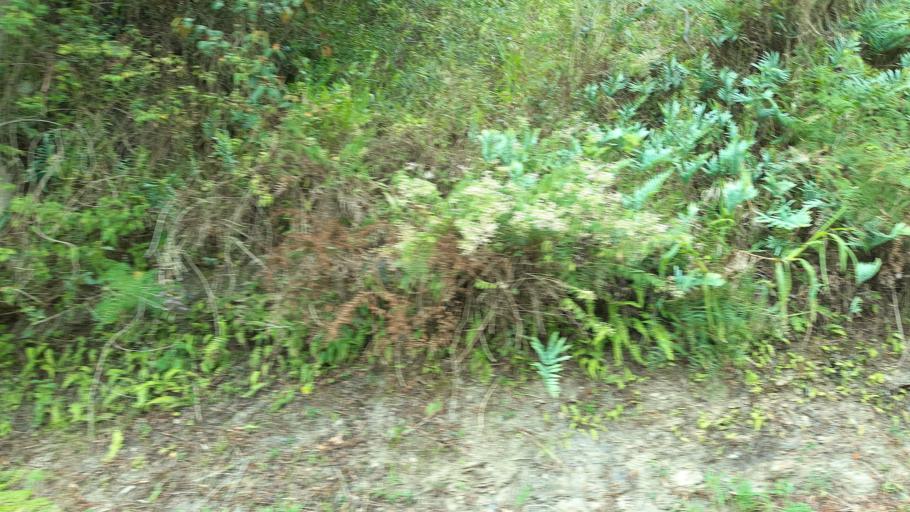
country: CO
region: Boyaca
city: Moniquira
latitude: 5.8434
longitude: -73.5831
